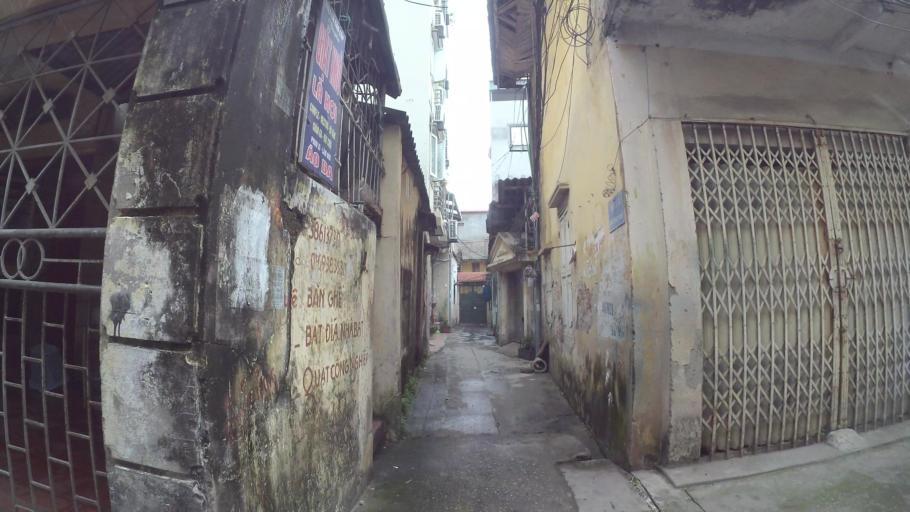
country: VN
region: Ha Noi
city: Van Dien
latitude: 20.9762
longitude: 105.8478
